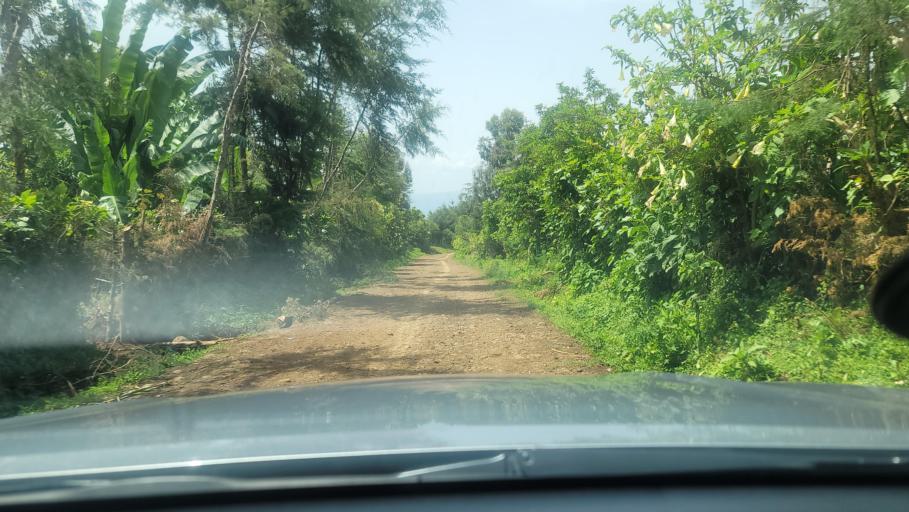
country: ET
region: Oromiya
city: Agaro
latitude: 7.8200
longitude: 36.4086
